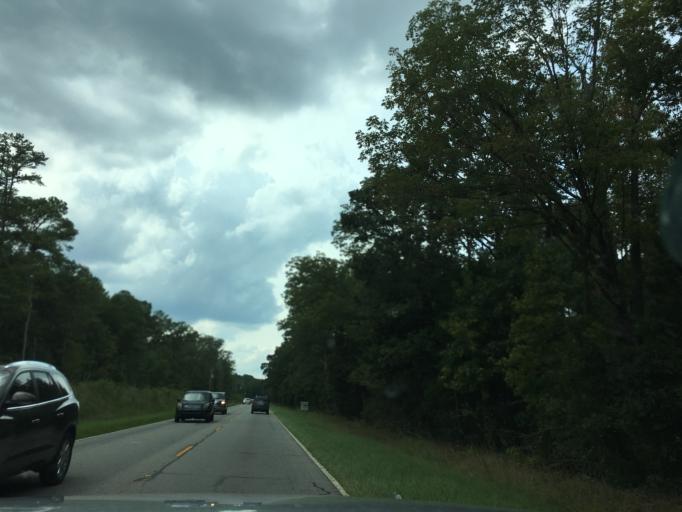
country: US
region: South Carolina
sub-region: Richland County
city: Lake Murray of Richland
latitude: 34.1619
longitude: -81.2596
